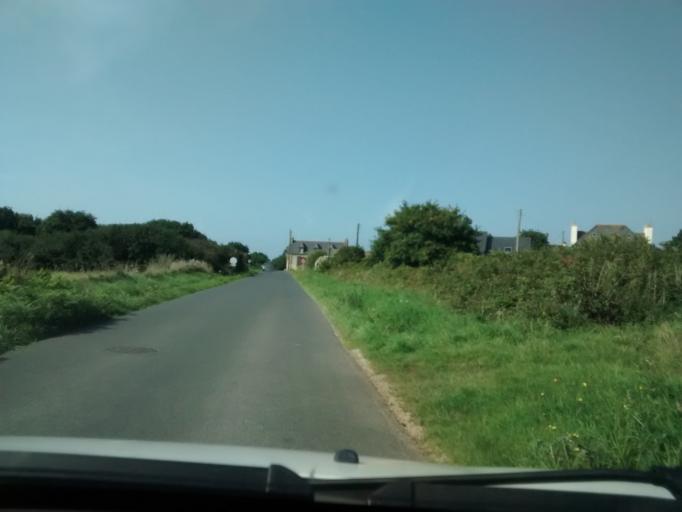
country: FR
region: Brittany
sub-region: Departement des Cotes-d'Armor
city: Penvenan
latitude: 48.8275
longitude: -3.3077
